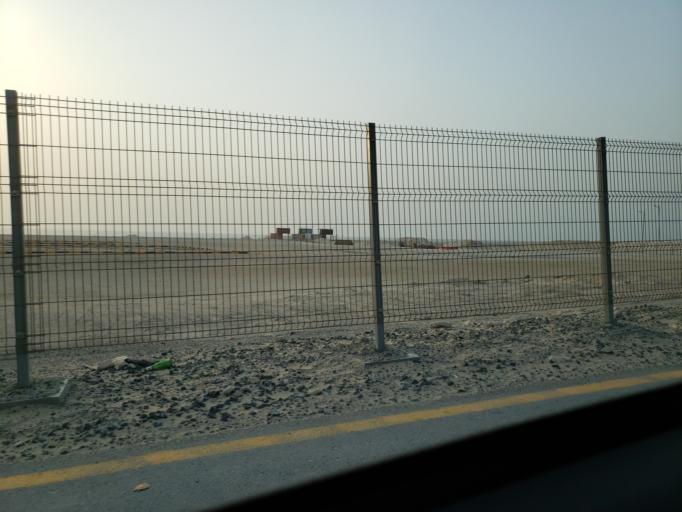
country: AE
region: Ajman
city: Ajman
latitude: 25.4299
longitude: 55.4584
